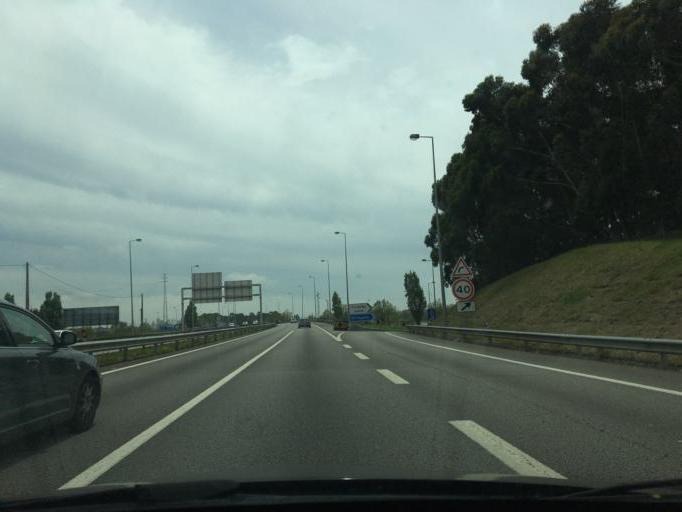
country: PT
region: Porto
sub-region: Matosinhos
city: Santa Cruz do Bispo
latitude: 41.2296
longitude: -8.6954
